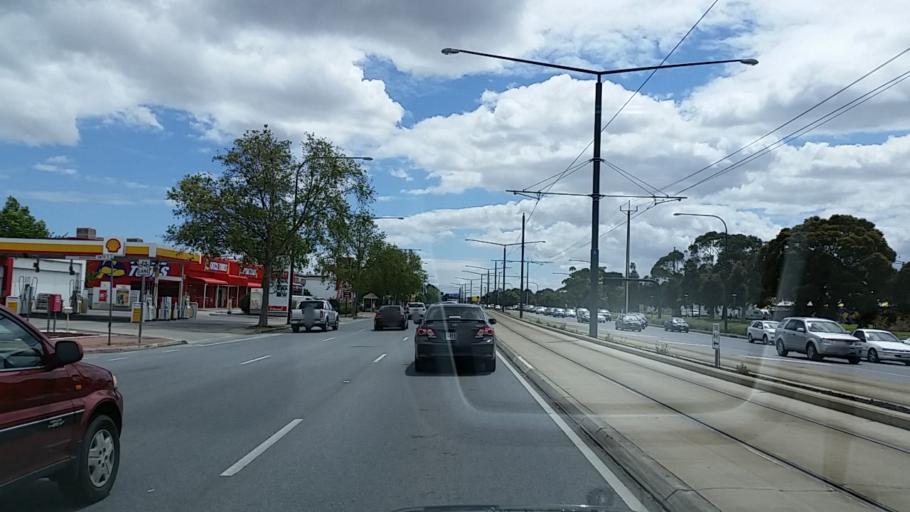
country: AU
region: South Australia
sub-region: City of West Torrens
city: Thebarton
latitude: -34.9155
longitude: 138.5781
